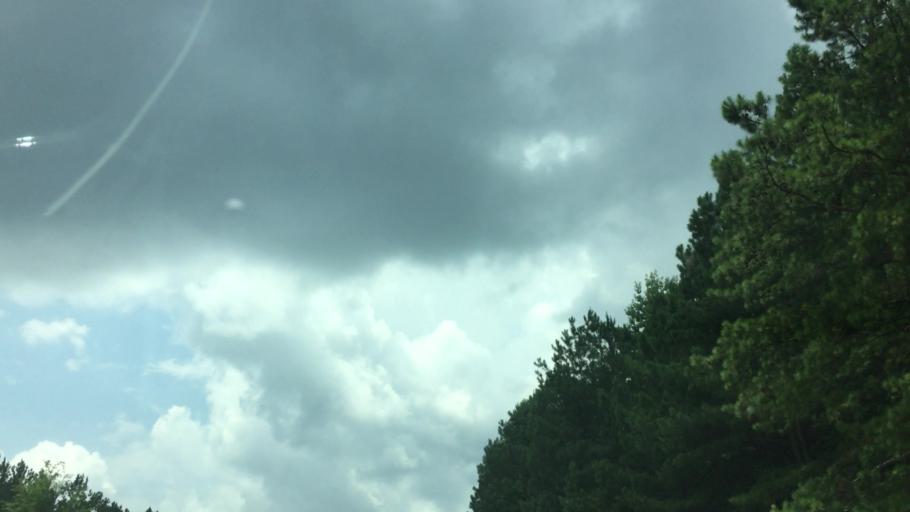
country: US
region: Georgia
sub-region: Fulton County
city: Fairburn
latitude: 33.6003
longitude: -84.6333
